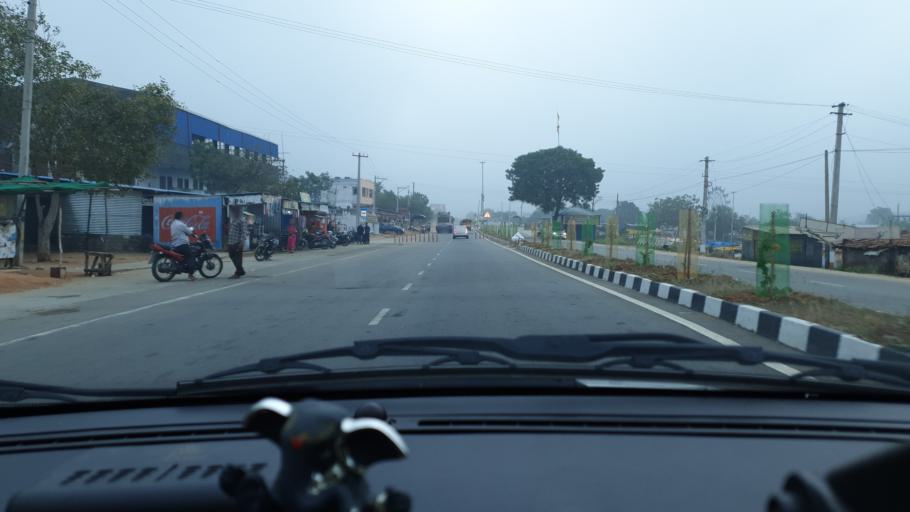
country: IN
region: Telangana
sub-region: Mahbubnagar
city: Farrukhnagar
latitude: 16.9551
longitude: 78.5164
